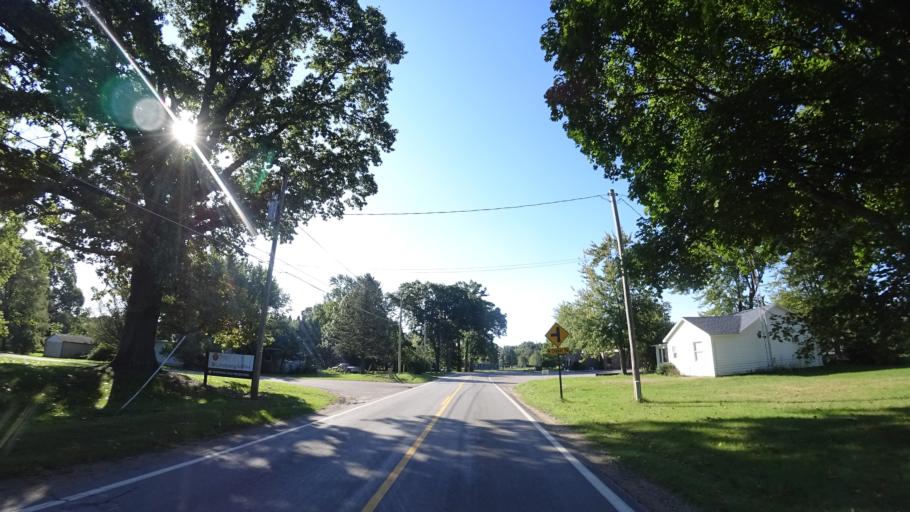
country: US
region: Michigan
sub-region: Berrien County
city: Lake Michigan Beach
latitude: 42.1809
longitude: -86.3835
